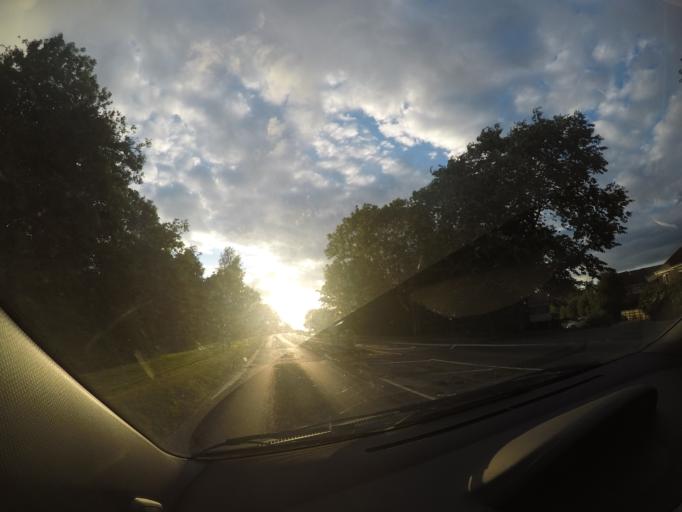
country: GB
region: England
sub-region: North Yorkshire
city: Catterick
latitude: 54.3795
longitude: -1.6354
